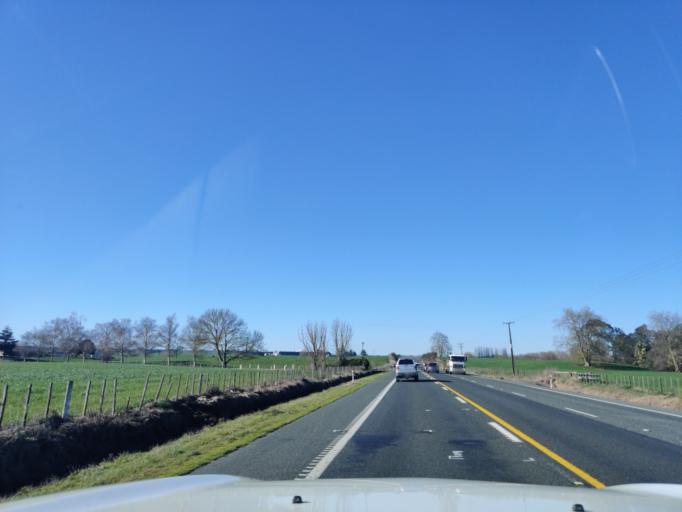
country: NZ
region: Waikato
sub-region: Matamata-Piako District
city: Matamata
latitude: -38.0208
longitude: 175.7832
